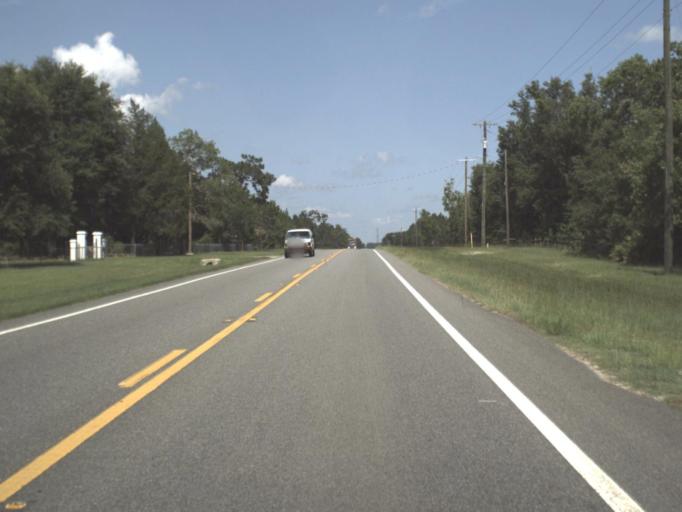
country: US
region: Florida
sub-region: Clay County
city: Asbury Lake
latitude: 29.9828
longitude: -81.7856
